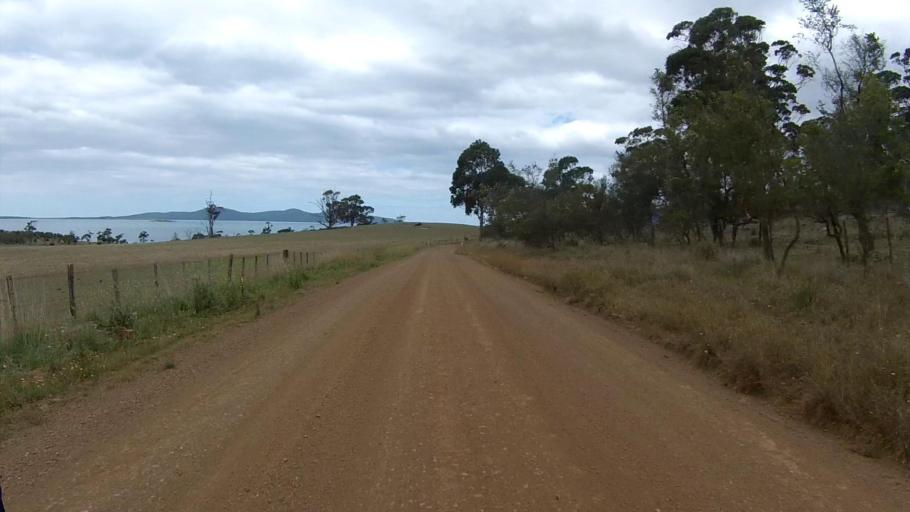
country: AU
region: Tasmania
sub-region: Sorell
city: Sorell
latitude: -42.6168
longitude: 147.9318
